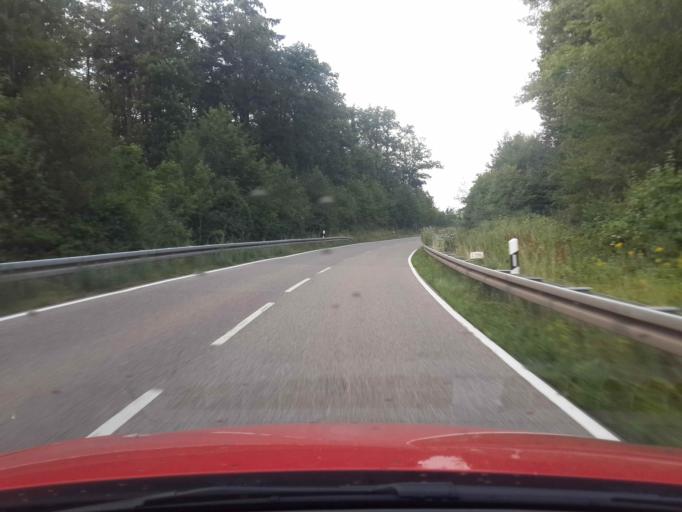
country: DE
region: Baden-Wuerttemberg
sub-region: Regierungsbezirk Stuttgart
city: Pfaffenhofen
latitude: 49.0504
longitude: 8.9877
